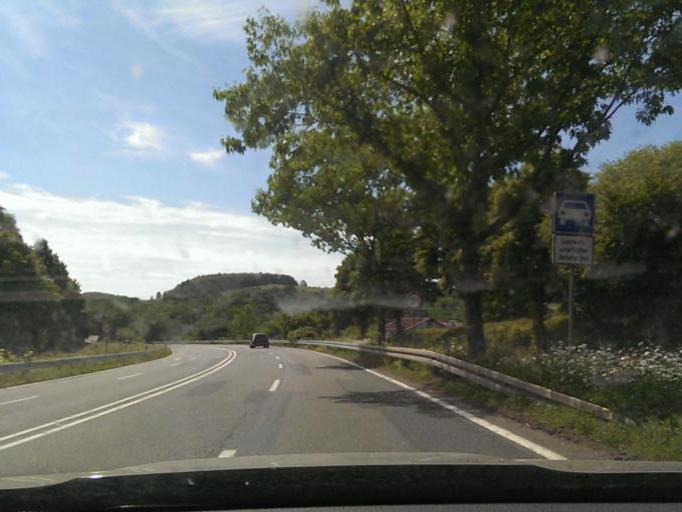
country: DE
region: Lower Saxony
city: Alfeld
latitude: 51.9902
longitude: 9.8000
